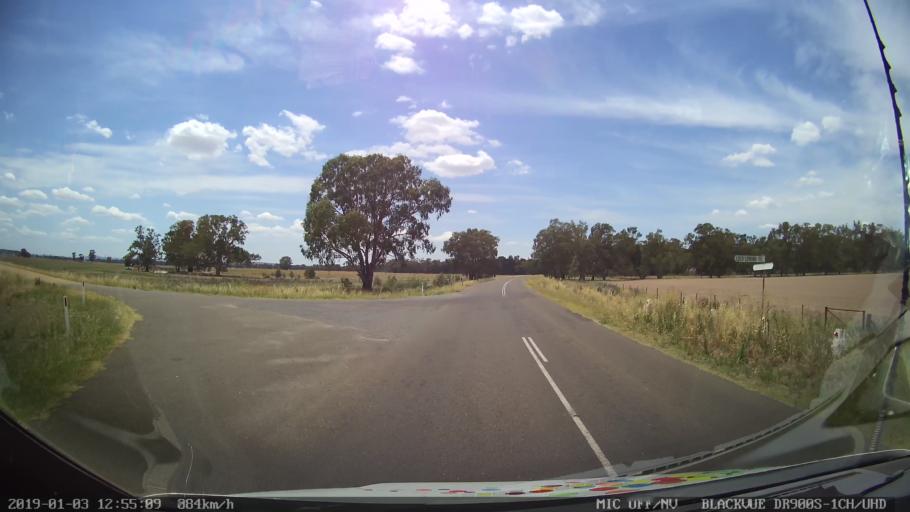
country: AU
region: New South Wales
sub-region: Weddin
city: Grenfell
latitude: -33.6465
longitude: 148.3262
